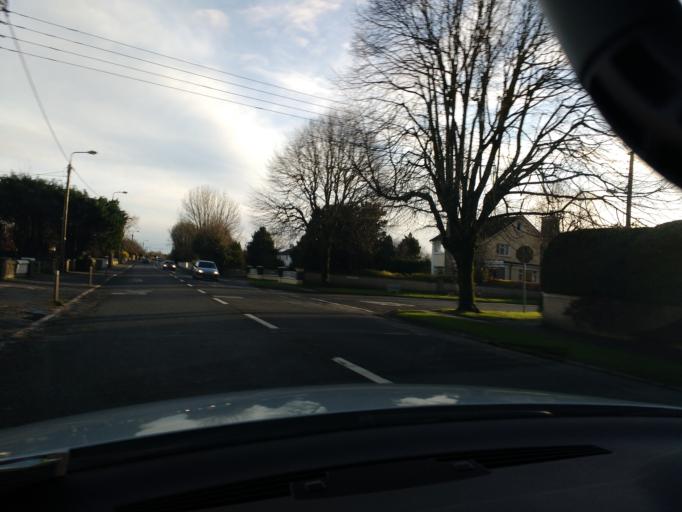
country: IE
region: Munster
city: Thurles
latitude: 52.6719
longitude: -7.8116
